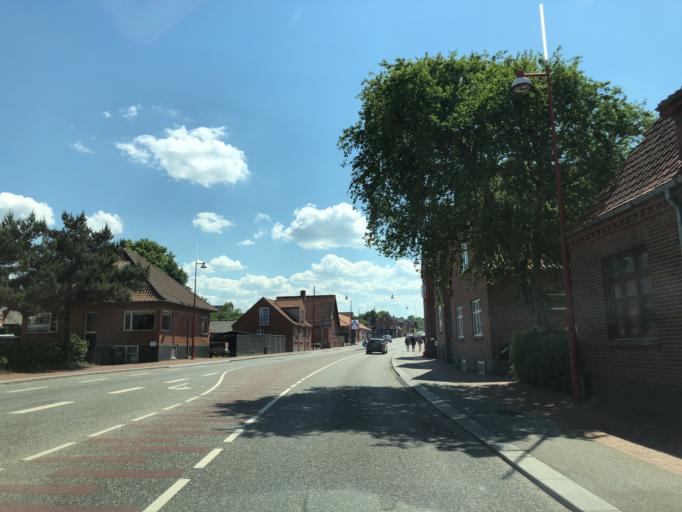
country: DK
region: Central Jutland
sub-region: Struer Kommune
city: Struer
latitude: 56.4929
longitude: 8.5837
